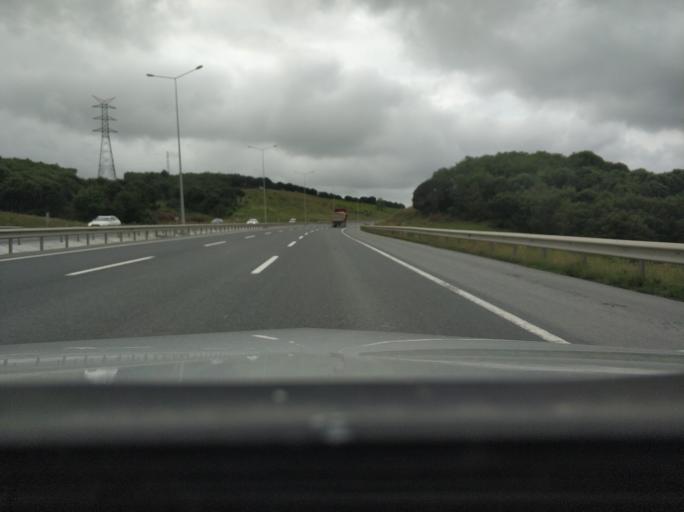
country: TR
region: Istanbul
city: Kemerburgaz
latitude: 41.1452
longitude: 28.9039
